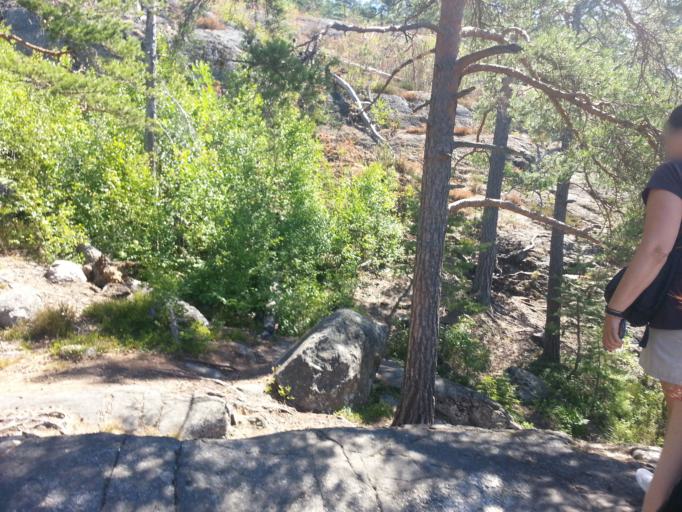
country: SE
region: Stockholm
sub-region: Tyreso Kommun
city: Bollmora
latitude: 59.2216
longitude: 18.2695
